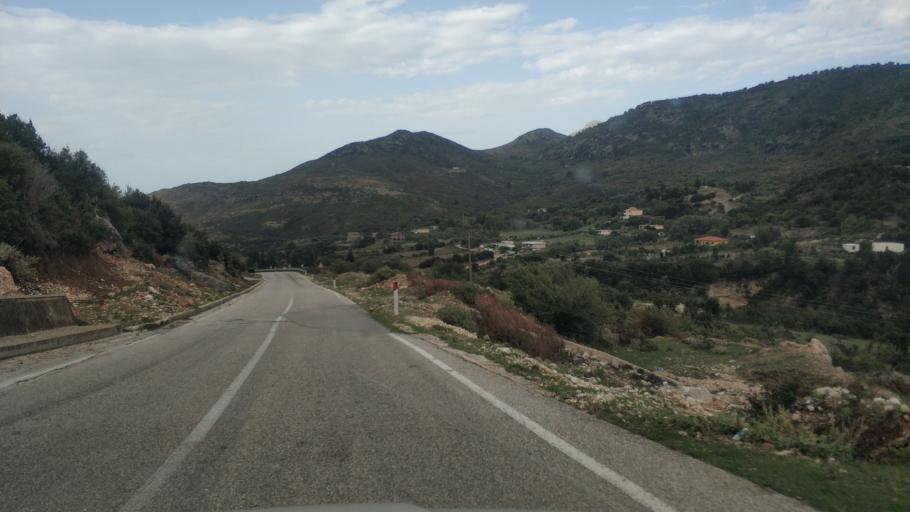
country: AL
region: Vlore
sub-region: Rrethi i Vlores
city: Orikum
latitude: 40.2667
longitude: 19.5160
